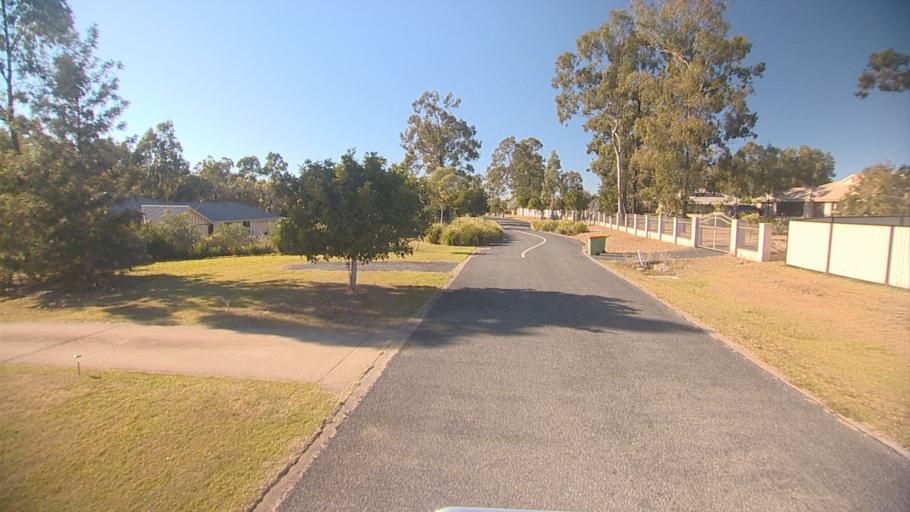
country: AU
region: Queensland
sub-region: Logan
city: North Maclean
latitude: -27.7468
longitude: 152.9593
